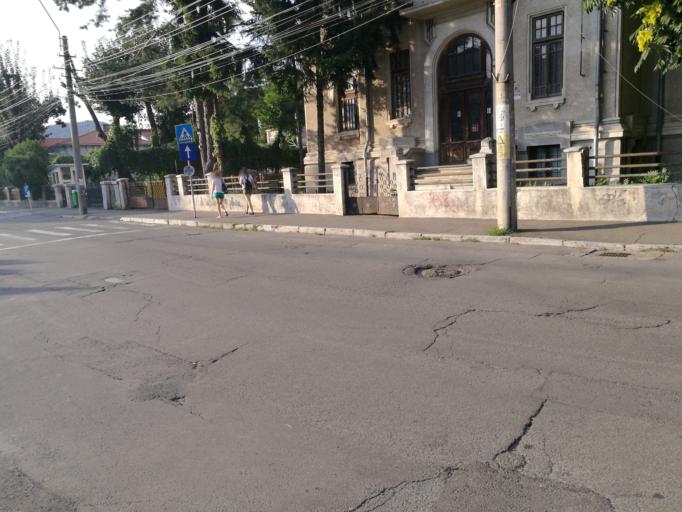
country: RO
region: Neamt
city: Piatra Neamt
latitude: 46.9331
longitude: 26.3655
